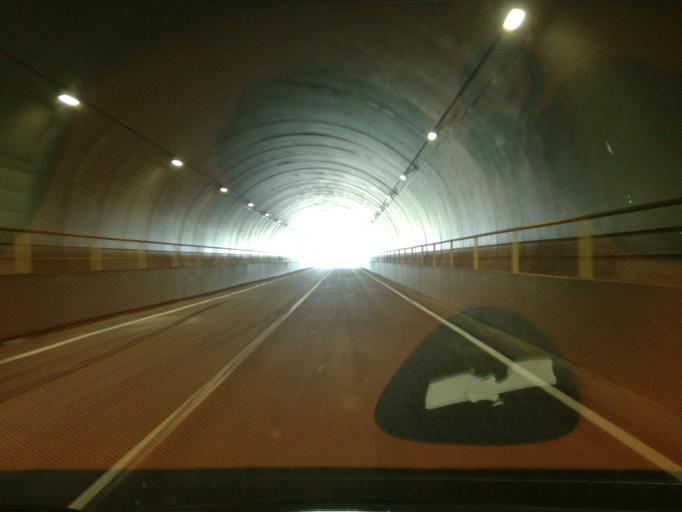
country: PT
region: Porto
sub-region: Trofa
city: Sao Romao do Coronado
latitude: 41.2827
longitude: -8.5195
